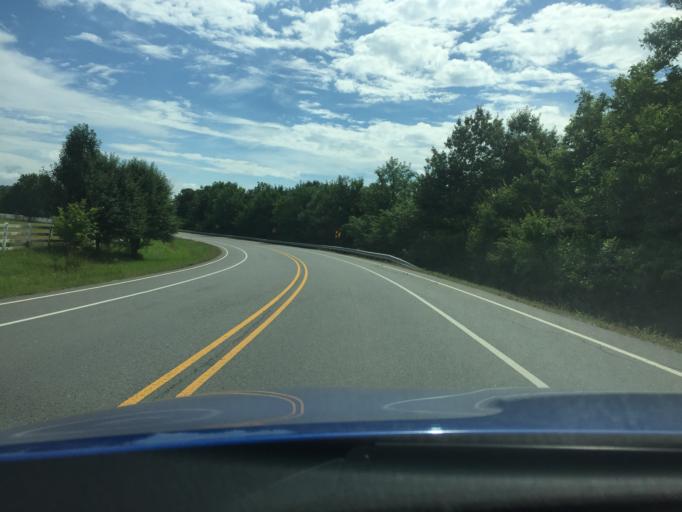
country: US
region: Arkansas
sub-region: Pulaski County
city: Maumelle
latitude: 34.8168
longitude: -92.4417
